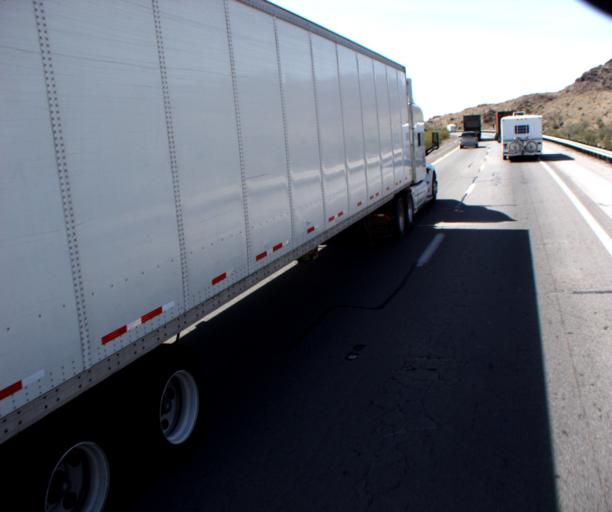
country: US
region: Arizona
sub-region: La Paz County
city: Ehrenberg
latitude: 33.6447
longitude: -114.3805
